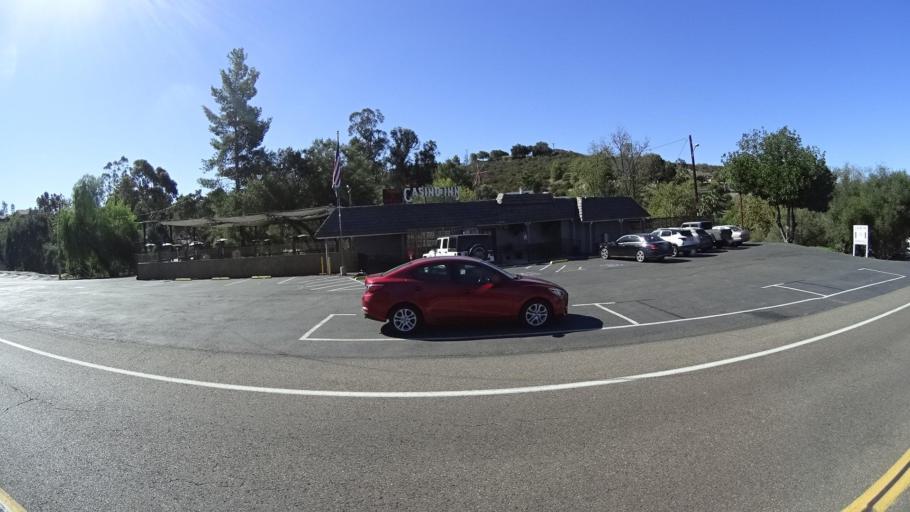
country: US
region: California
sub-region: San Diego County
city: Alpine
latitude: 32.8399
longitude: -116.7898
